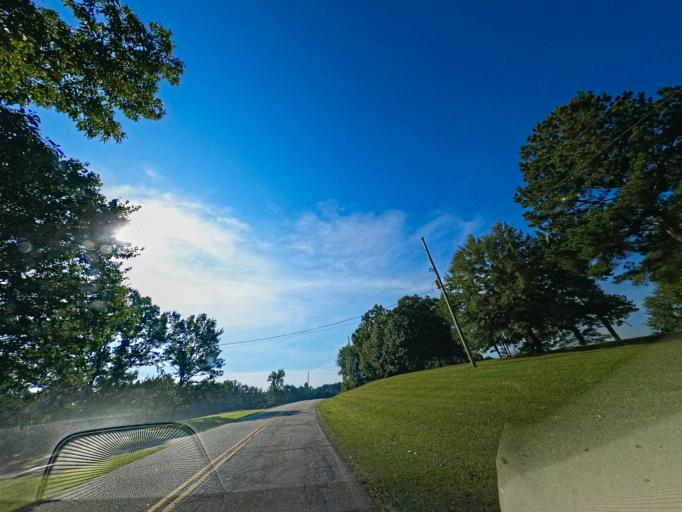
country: US
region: Georgia
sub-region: Coweta County
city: Grantville
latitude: 33.2906
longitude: -84.9301
